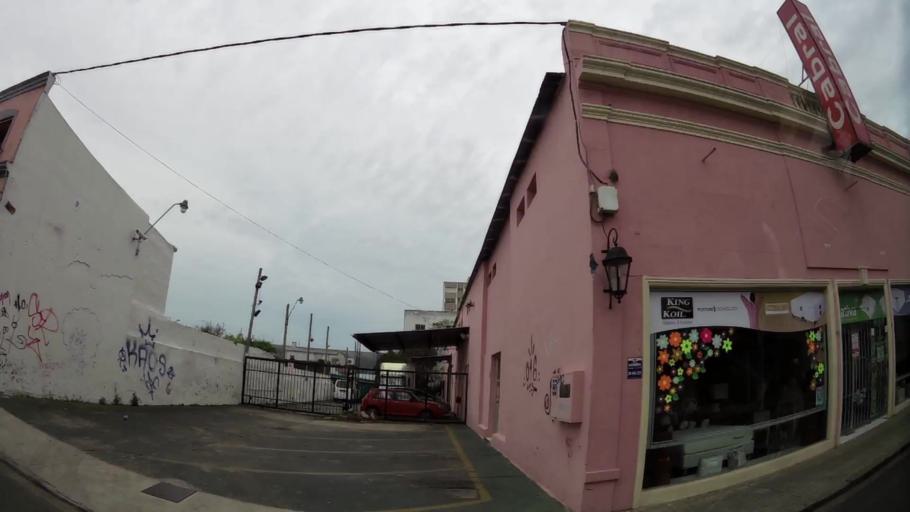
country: UY
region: Maldonado
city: Maldonado
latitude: -34.9059
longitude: -54.9588
